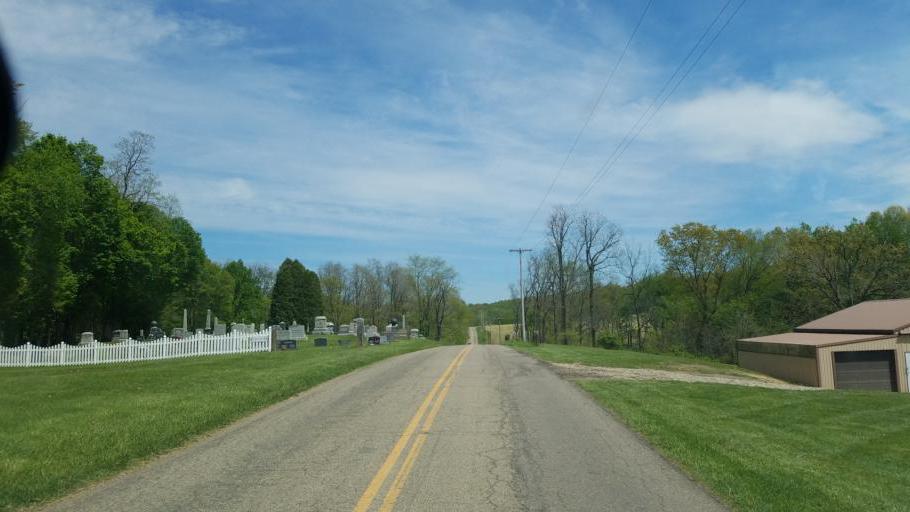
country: US
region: Ohio
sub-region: Knox County
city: Gambier
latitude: 40.3751
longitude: -82.3526
